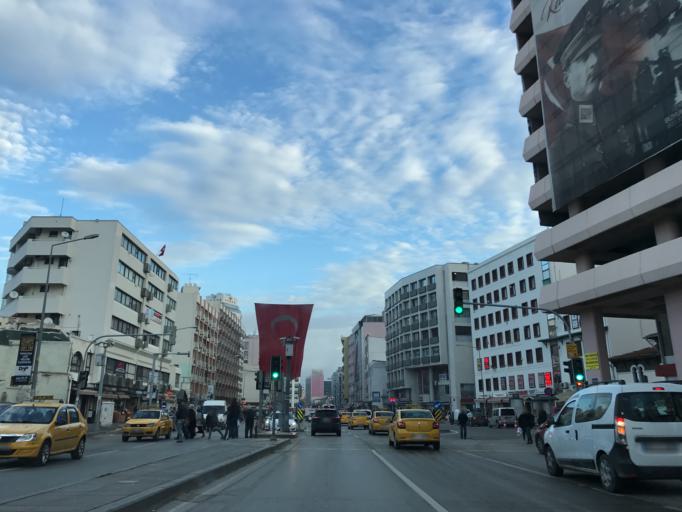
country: TR
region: Izmir
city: Izmir
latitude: 38.4200
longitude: 27.1369
